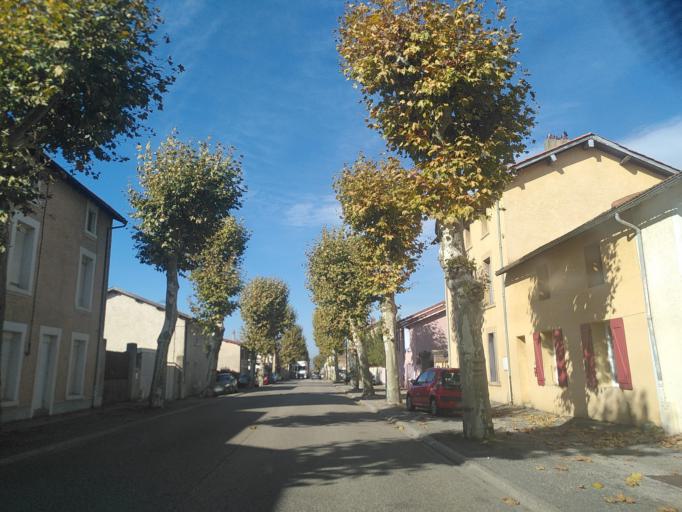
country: FR
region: Rhone-Alpes
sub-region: Departement de l'Isere
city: Chanas
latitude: 45.2848
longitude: 4.8179
